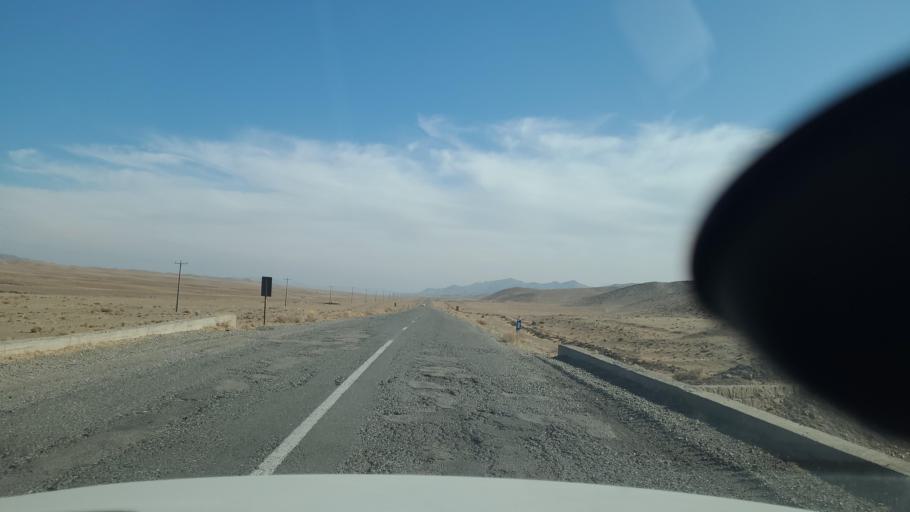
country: IR
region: Razavi Khorasan
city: Fariman
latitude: 35.5910
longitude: 59.6071
